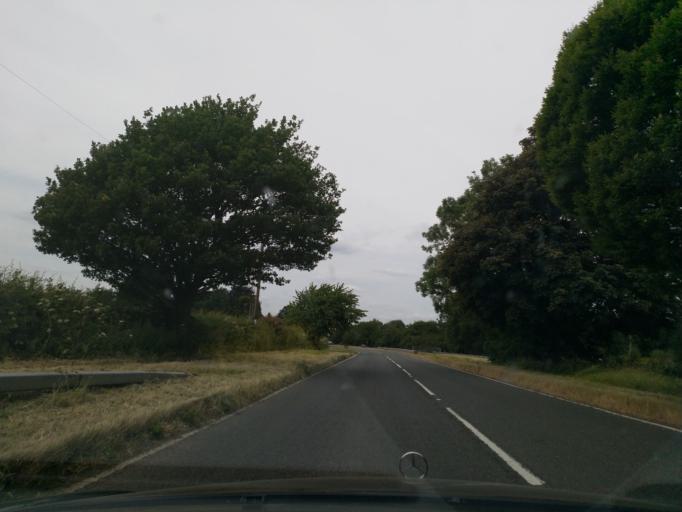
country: GB
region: England
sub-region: Solihull
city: Balsall Common
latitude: 52.4089
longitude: -1.6648
